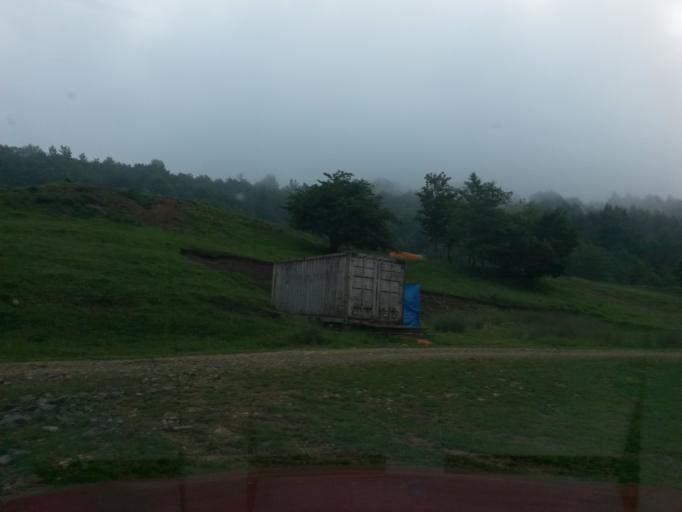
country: UA
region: Zakarpattia
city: Velykyi Bereznyi
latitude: 48.9104
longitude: 22.4831
